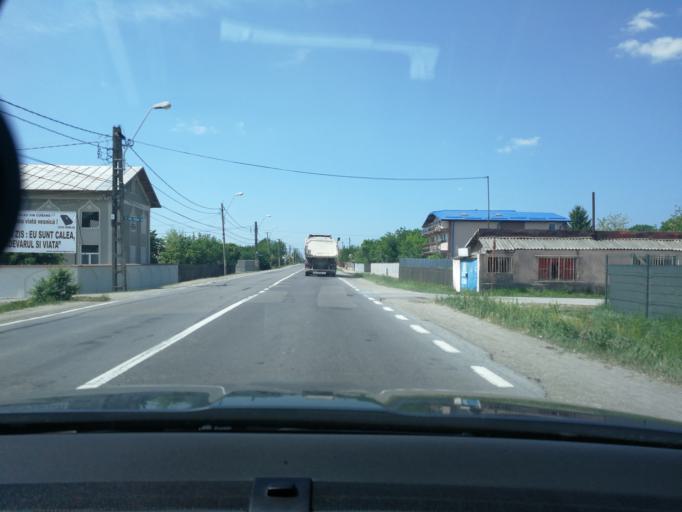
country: RO
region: Prahova
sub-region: Comuna Brazi
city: Negoiesti
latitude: 44.9074
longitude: 25.9878
